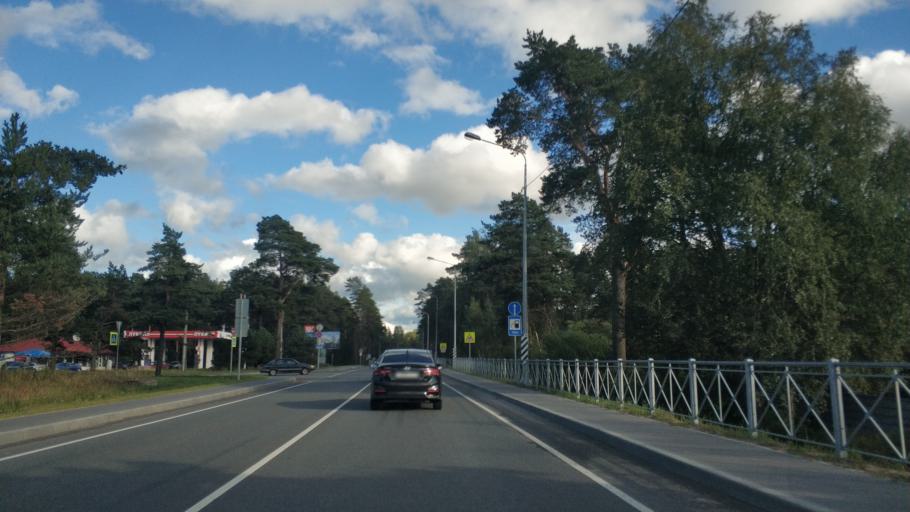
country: RU
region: Leningrad
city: Priozersk
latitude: 61.0195
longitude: 30.1339
